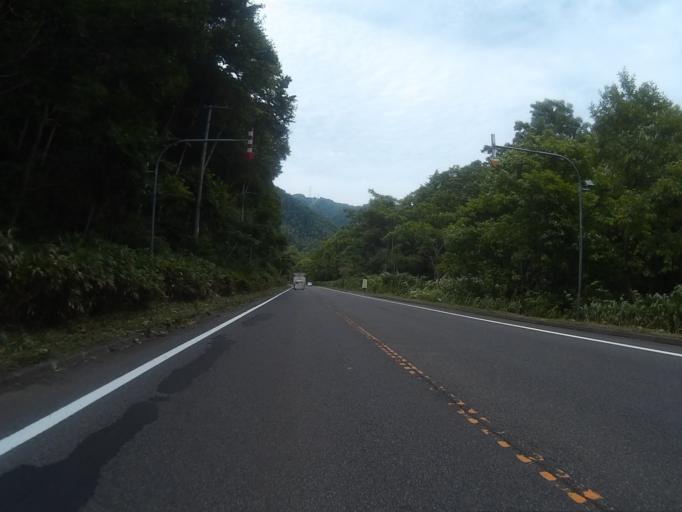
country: JP
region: Hokkaido
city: Sapporo
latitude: 42.9228
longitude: 141.1221
